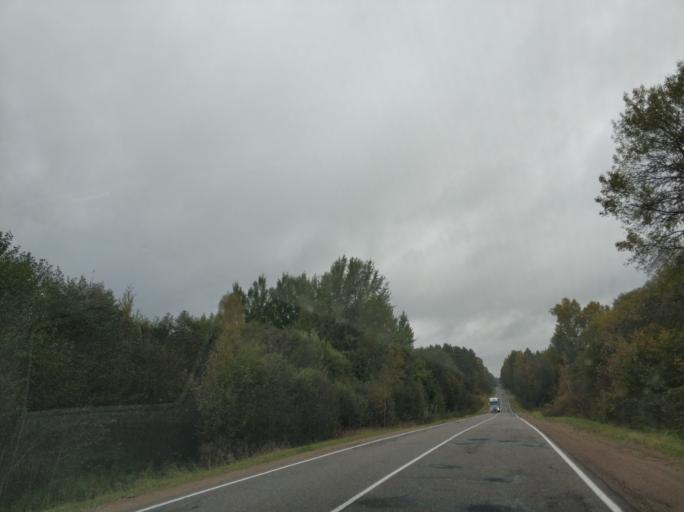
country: RU
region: Pskov
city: Opochka
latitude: 56.5612
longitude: 28.6275
